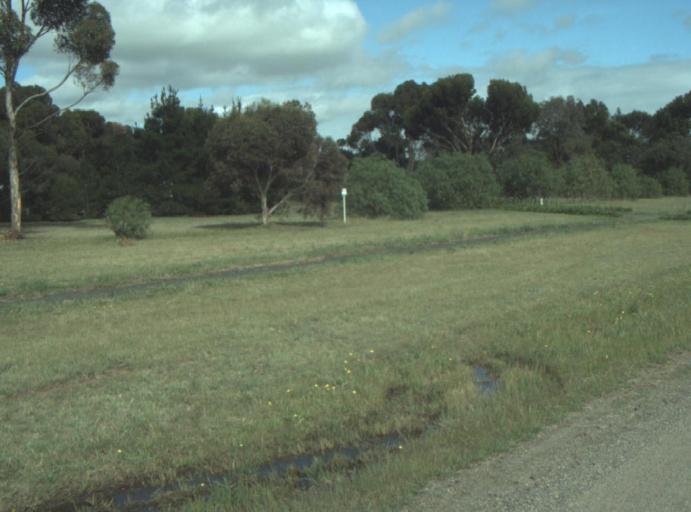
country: AU
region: Victoria
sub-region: Greater Geelong
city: Lara
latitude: -38.0140
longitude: 144.3879
